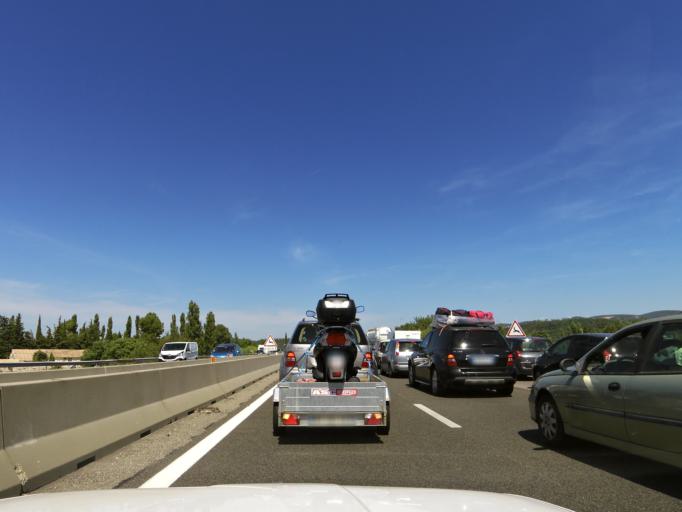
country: FR
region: Rhone-Alpes
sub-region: Departement de la Drome
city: La Garde-Adhemar
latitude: 44.4102
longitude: 4.7300
